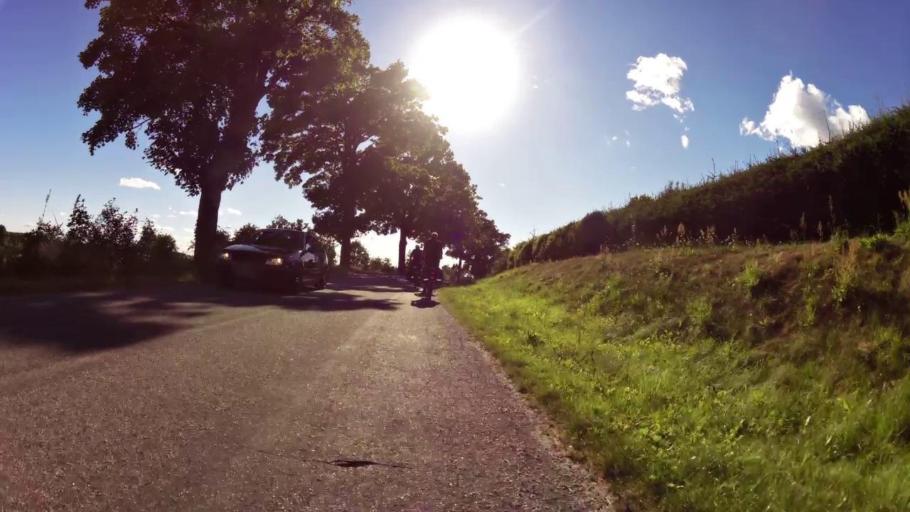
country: PL
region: West Pomeranian Voivodeship
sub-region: Powiat swidwinski
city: Swidwin
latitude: 53.7749
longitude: 15.7512
